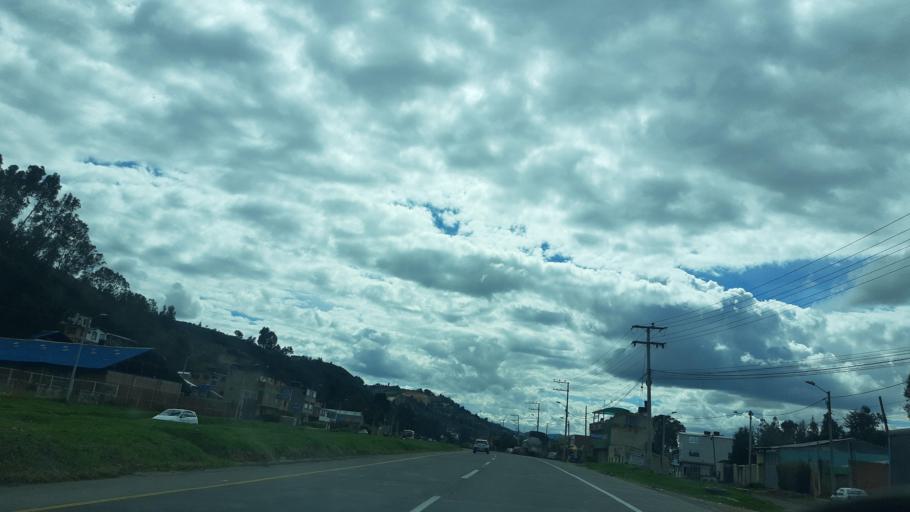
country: CO
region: Cundinamarca
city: Gachancipa
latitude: 4.9780
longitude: -73.8904
